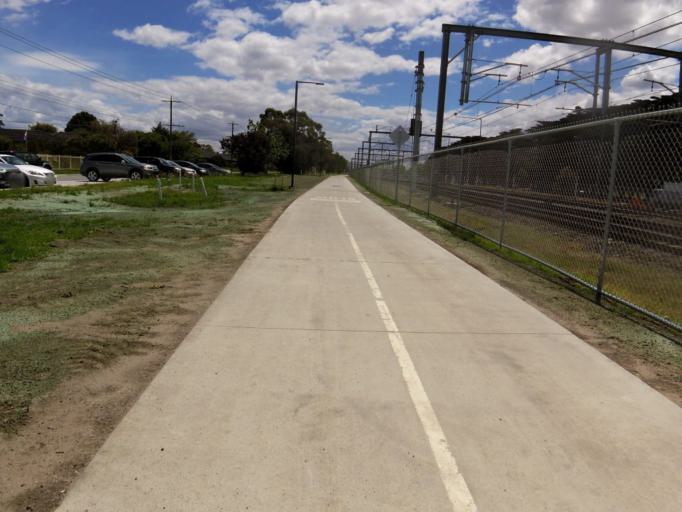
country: AU
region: Victoria
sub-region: Greater Dandenong
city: Springvale
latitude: -37.9457
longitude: 145.1483
